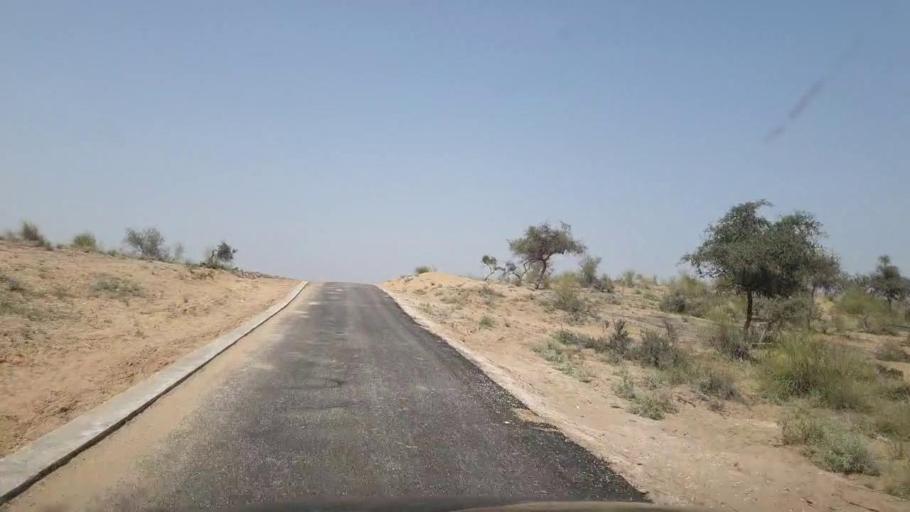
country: PK
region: Sindh
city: Islamkot
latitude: 25.1180
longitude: 70.6521
